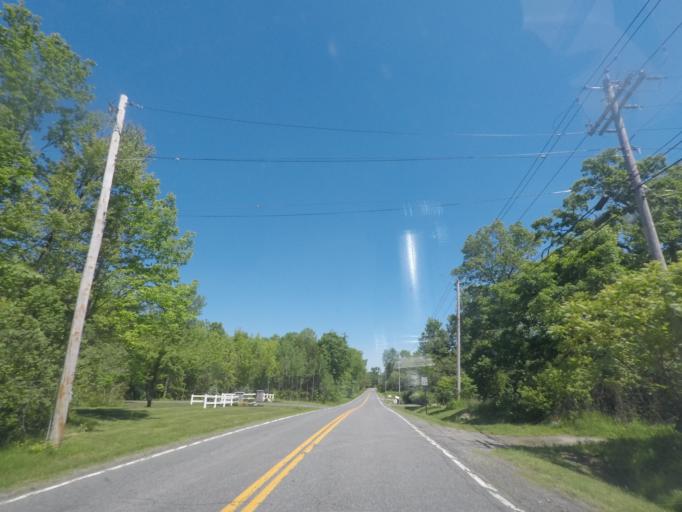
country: US
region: New York
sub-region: Schenectady County
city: East Glenville
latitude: 42.8789
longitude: -73.8649
